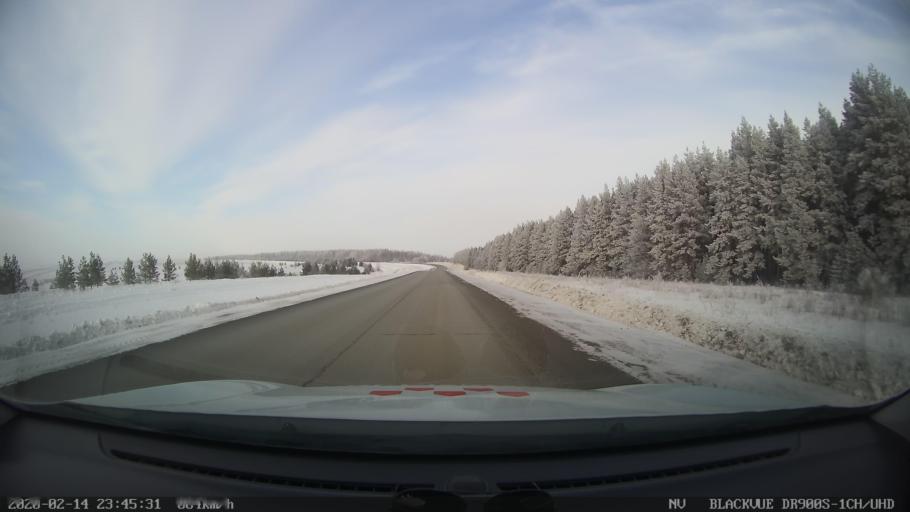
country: RU
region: Tatarstan
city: Kuybyshevskiy Zaton
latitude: 55.2218
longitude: 49.2325
